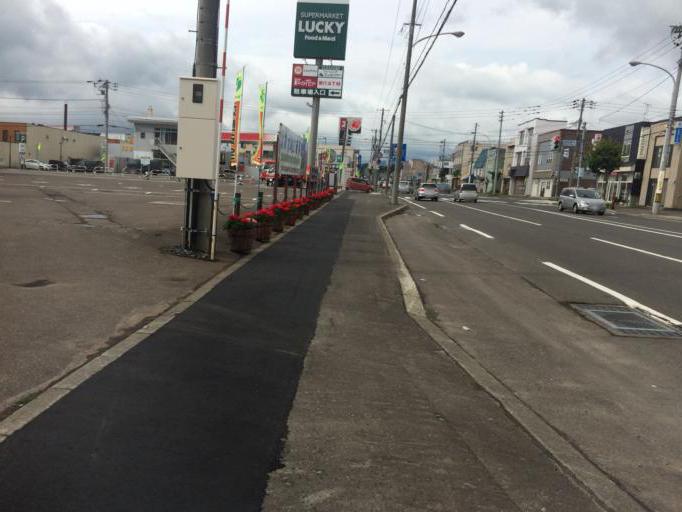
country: JP
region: Hokkaido
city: Niseko Town
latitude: 42.8998
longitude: 140.7523
